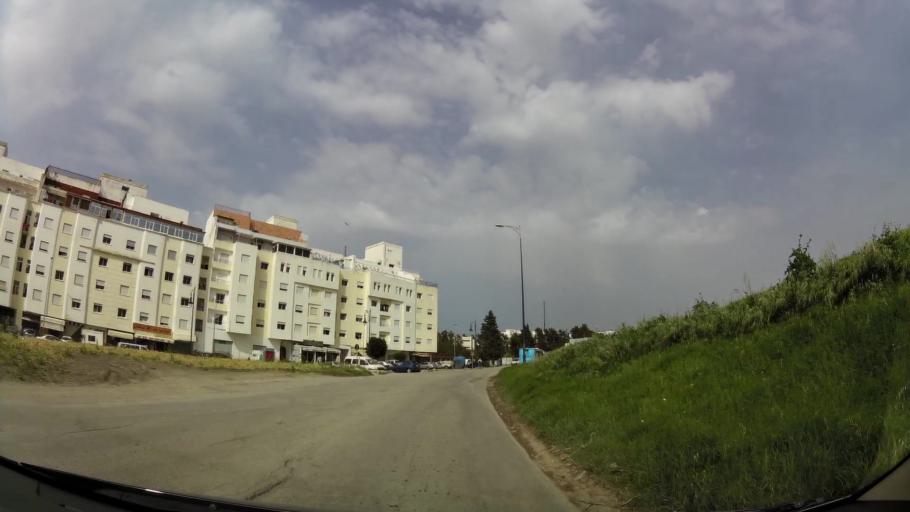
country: MA
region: Tanger-Tetouan
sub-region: Tanger-Assilah
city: Boukhalef
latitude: 35.7340
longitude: -5.8935
